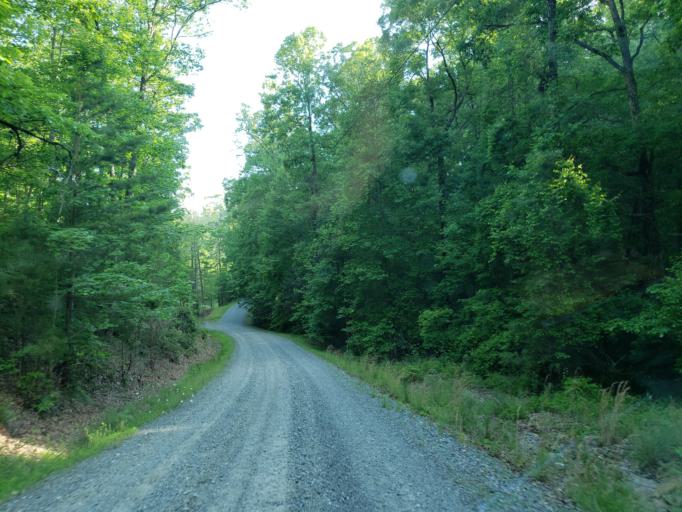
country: US
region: Georgia
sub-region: Gilmer County
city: Ellijay
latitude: 34.6478
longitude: -84.6451
